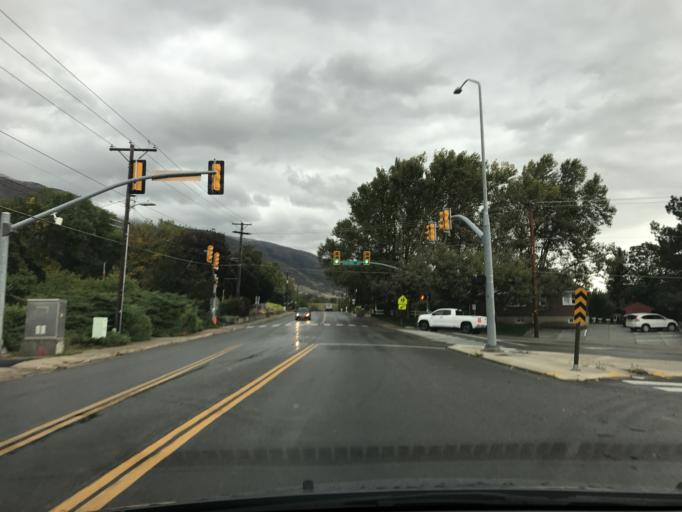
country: US
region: Utah
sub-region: Davis County
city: Farmington
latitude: 41.0011
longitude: -111.9008
